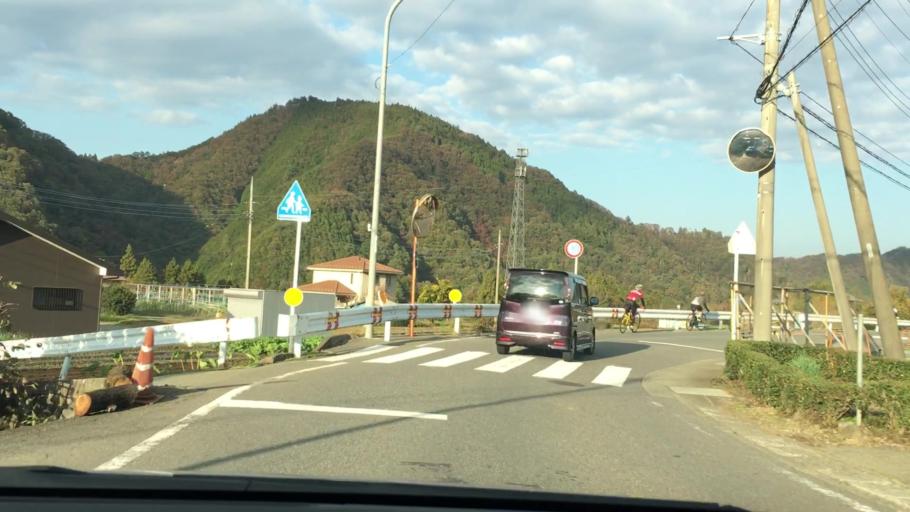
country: JP
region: Yamanashi
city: Uenohara
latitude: 35.5458
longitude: 139.1288
